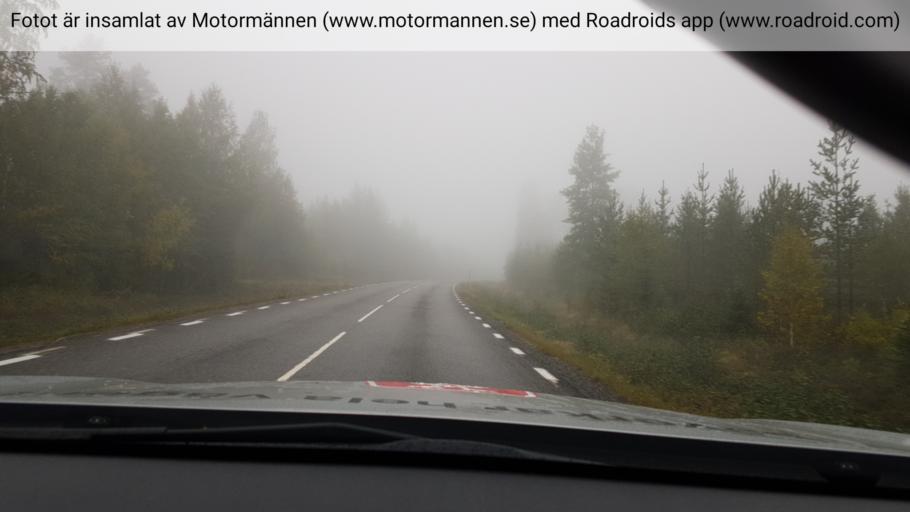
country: SE
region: Vaesterbotten
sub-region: Umea Kommun
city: Ersmark
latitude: 64.1194
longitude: 20.1630
